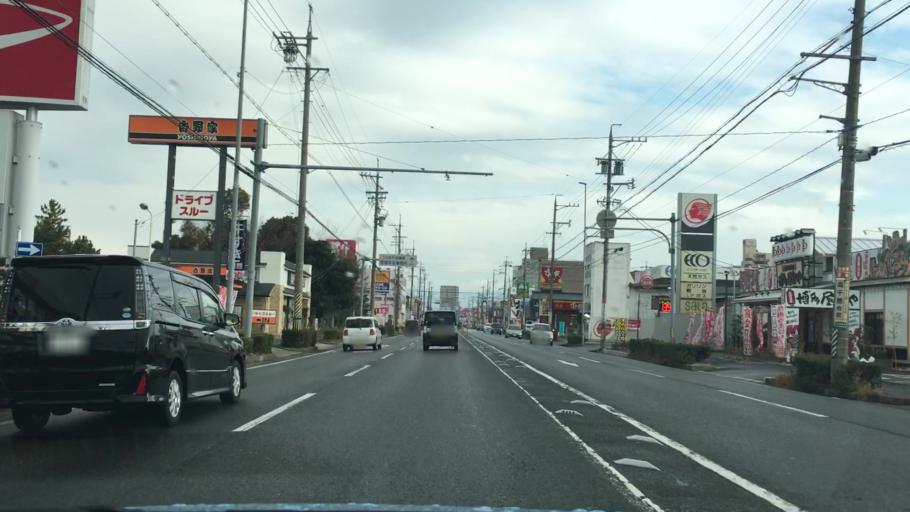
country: JP
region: Aichi
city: Toyohashi
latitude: 34.7675
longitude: 137.3710
